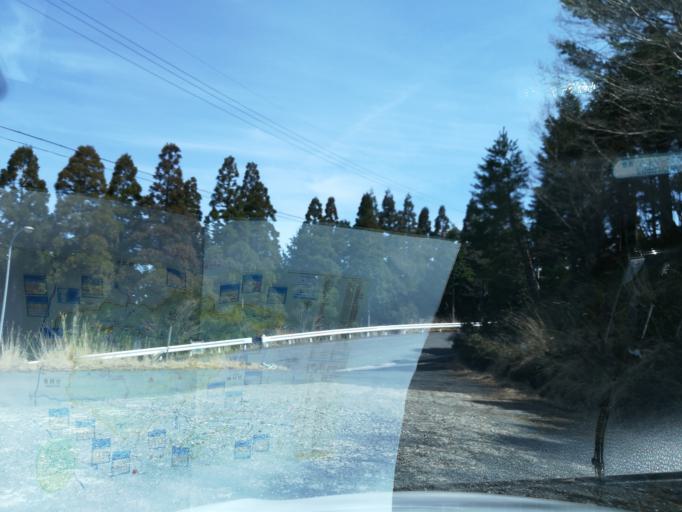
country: JP
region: Tokushima
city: Wakimachi
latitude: 33.8776
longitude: 134.0589
